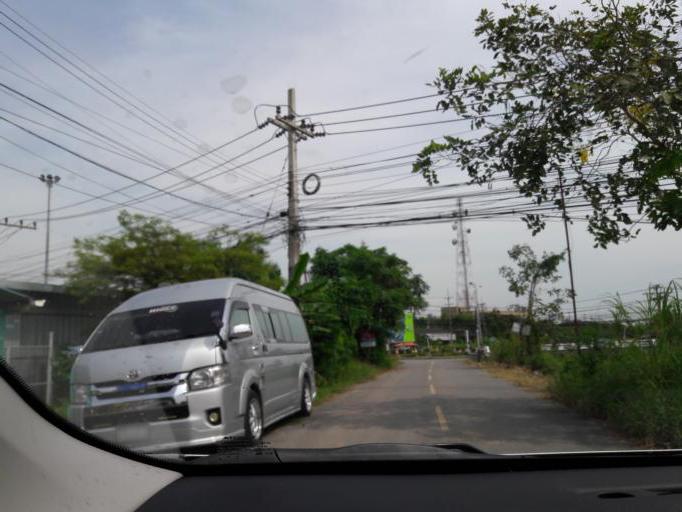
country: TH
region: Ang Thong
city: Ang Thong
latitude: 14.5845
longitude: 100.4552
